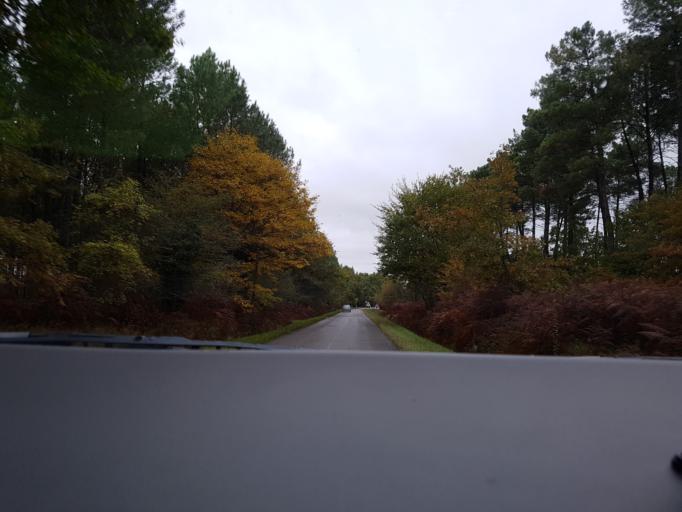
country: FR
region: Aquitaine
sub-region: Departement des Landes
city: Roquefort
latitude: 44.0568
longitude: -0.3485
